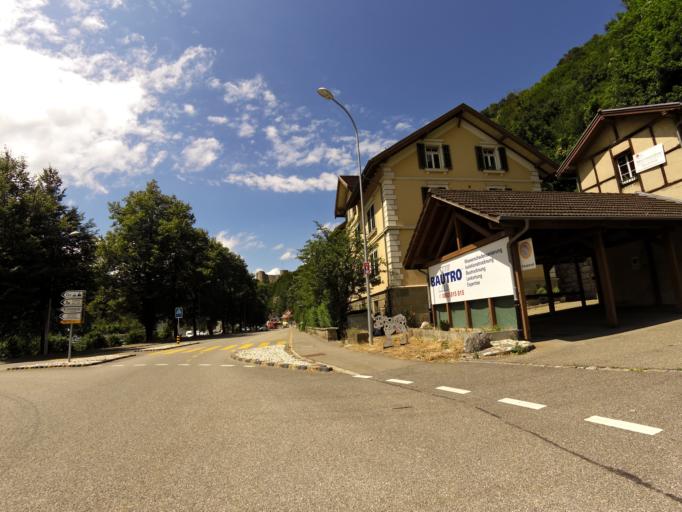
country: CH
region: Solothurn
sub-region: Bezirk Thal
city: Balsthal
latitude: 47.3047
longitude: 7.6947
